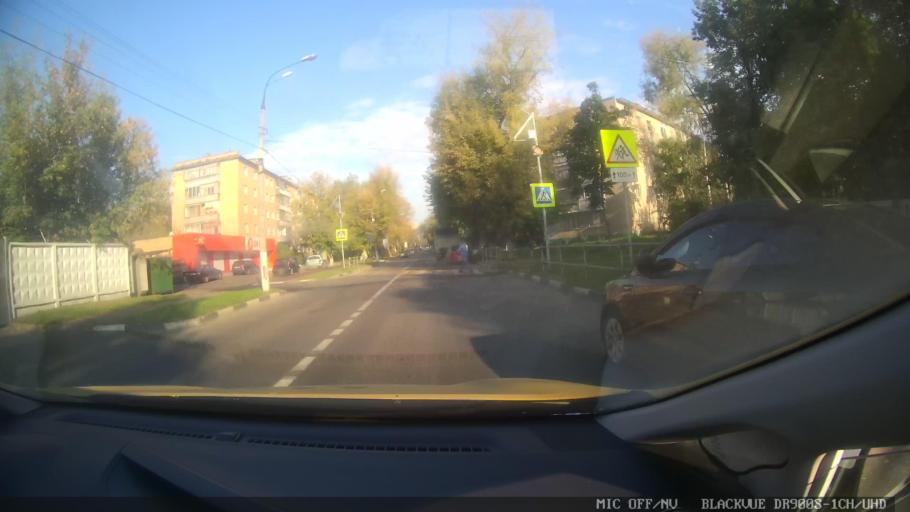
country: RU
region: Moskovskaya
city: Lyubertsy
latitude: 55.6743
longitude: 37.8873
